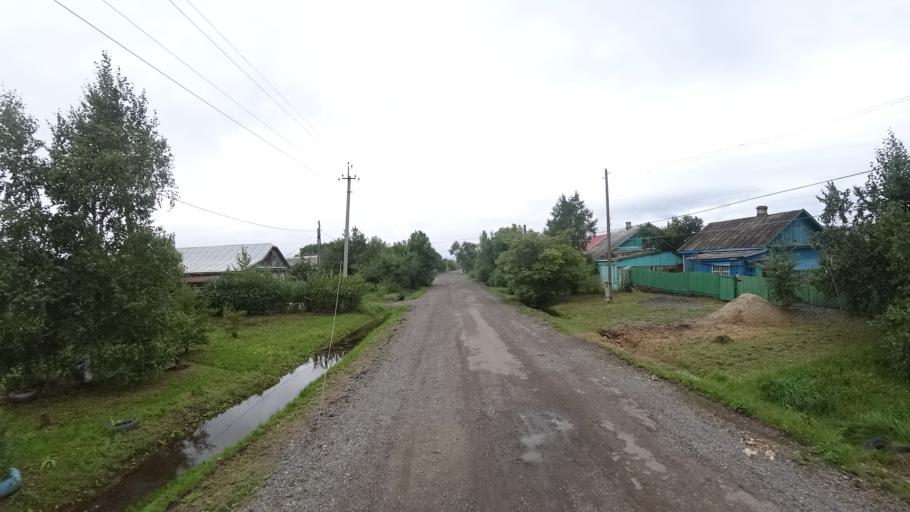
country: RU
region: Primorskiy
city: Chernigovka
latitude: 44.3470
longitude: 132.5786
